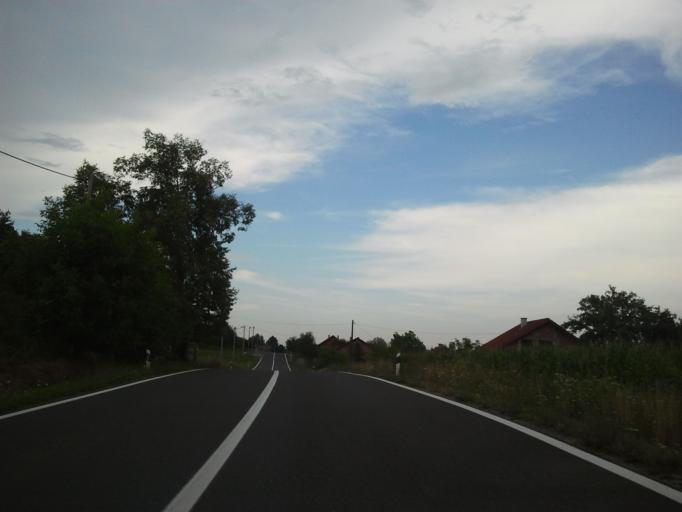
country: HR
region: Sisacko-Moslavacka
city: Glina
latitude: 45.3338
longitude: 16.0067
